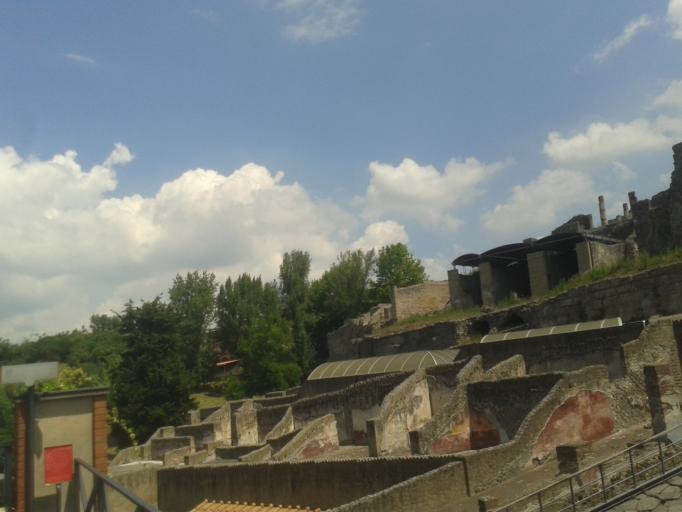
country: IT
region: Campania
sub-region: Provincia di Napoli
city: Pompei
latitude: 40.7484
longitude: 14.4828
